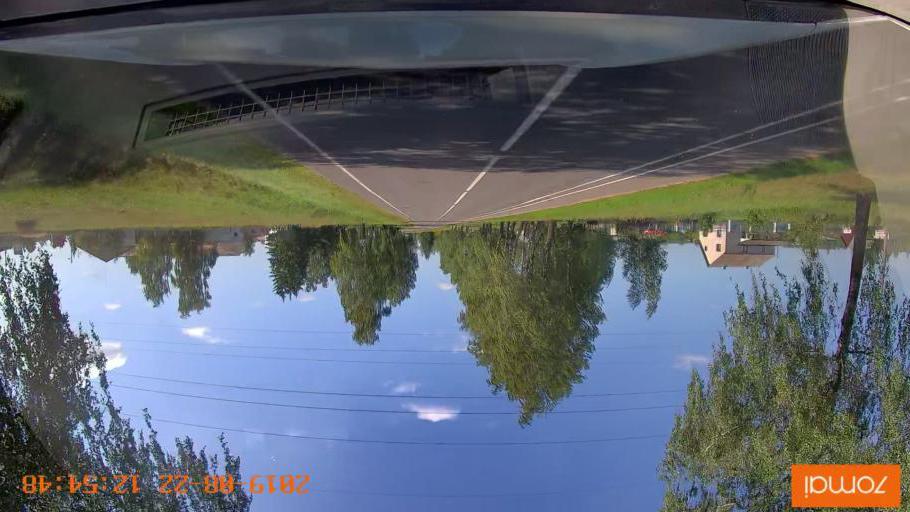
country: BY
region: Minsk
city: Prawdzinski
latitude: 53.4383
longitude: 27.7008
